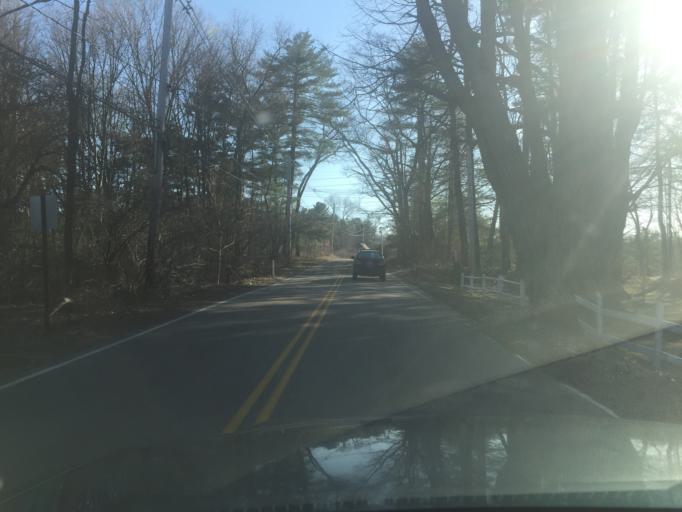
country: US
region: Massachusetts
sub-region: Norfolk County
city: Millis-Clicquot
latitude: 42.1350
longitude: -71.3590
